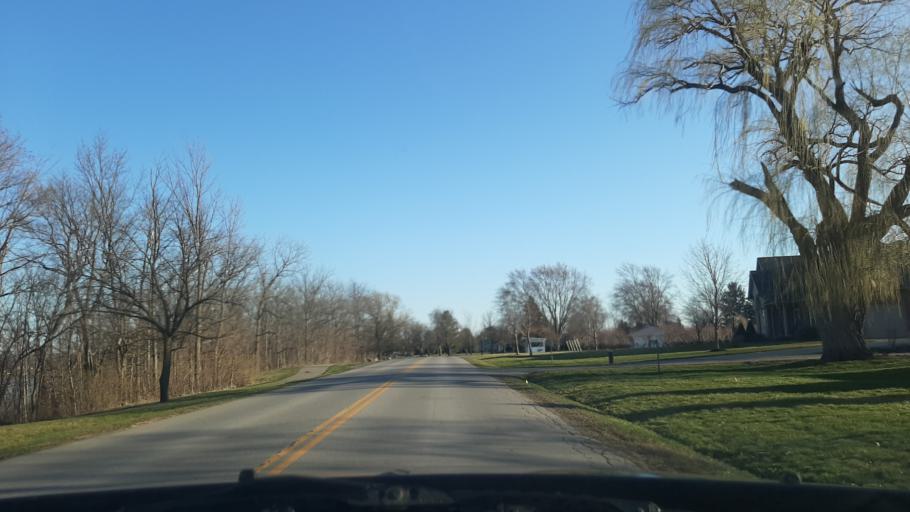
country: US
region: New York
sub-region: Niagara County
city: Youngstown
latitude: 43.2096
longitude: -79.0611
